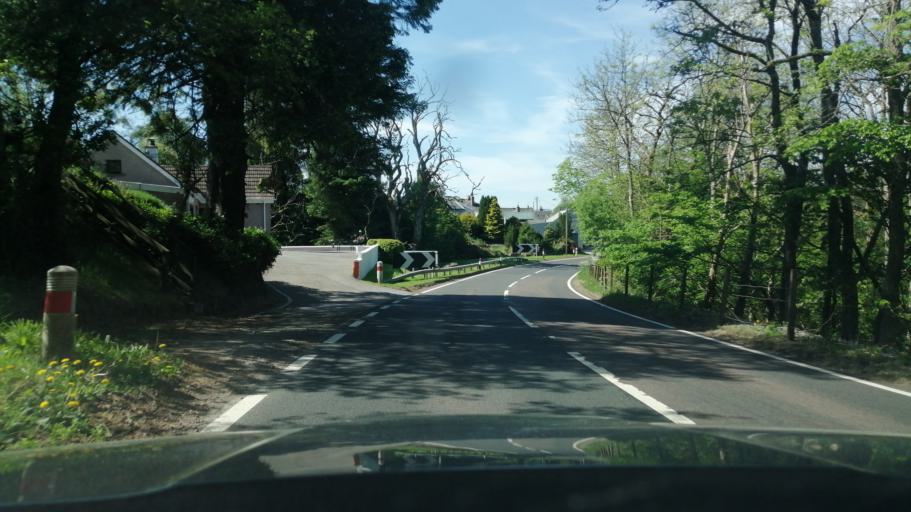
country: GB
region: Scotland
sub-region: Moray
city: Dufftown
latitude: 57.4992
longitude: -3.1384
